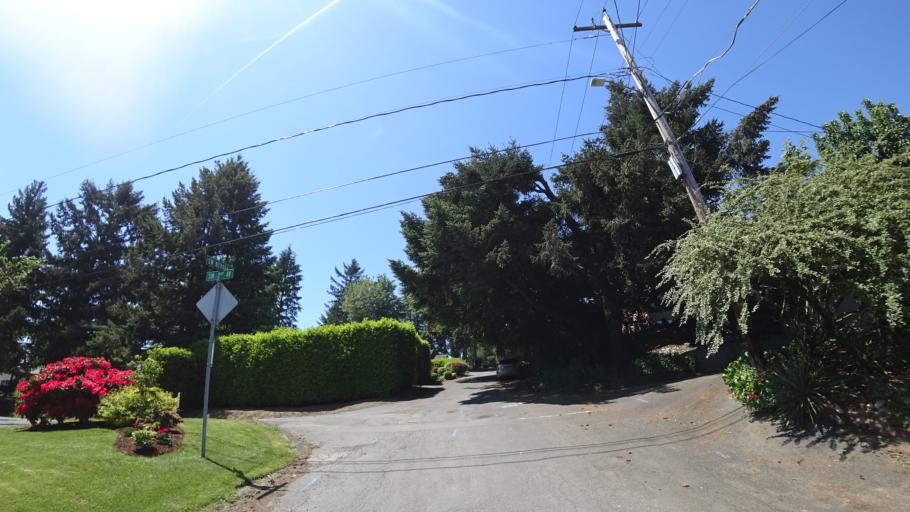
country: US
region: Oregon
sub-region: Clackamas County
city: Milwaukie
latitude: 45.4731
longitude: -122.6803
